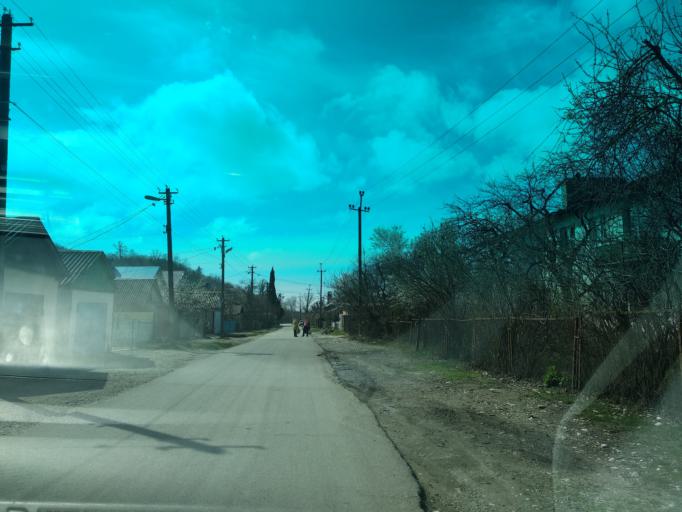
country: RU
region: Krasnodarskiy
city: Shepsi
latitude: 44.0501
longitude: 39.1603
